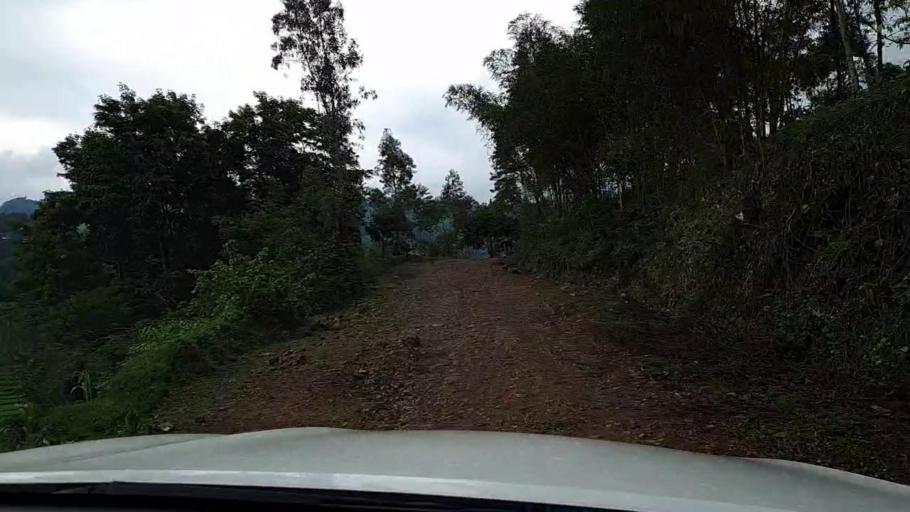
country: RW
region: Western Province
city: Cyangugu
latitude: -2.5592
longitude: 29.0354
